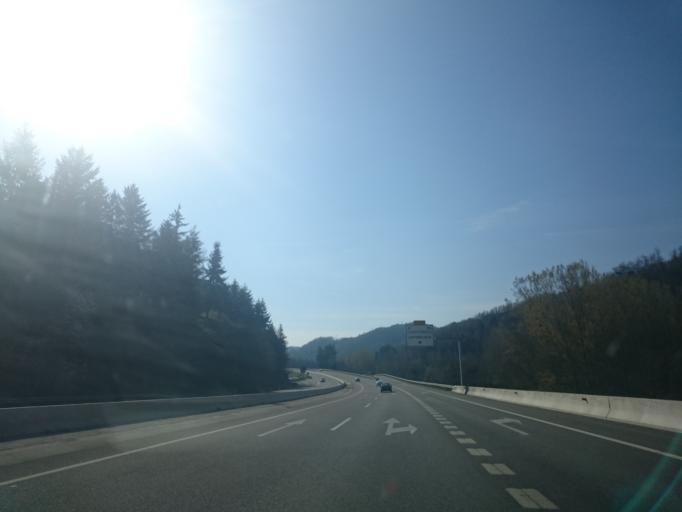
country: ES
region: Catalonia
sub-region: Provincia de Girona
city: Viladrau
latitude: 41.8769
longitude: 2.4009
